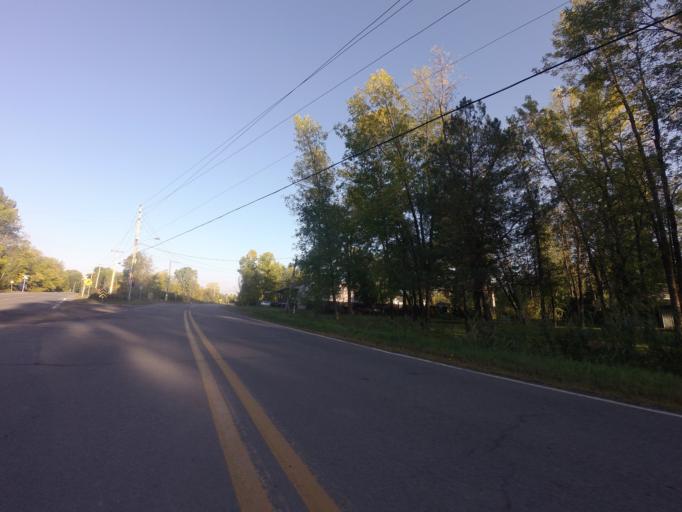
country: CA
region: Quebec
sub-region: Monteregie
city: Rigaud
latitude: 45.4806
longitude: -74.2547
